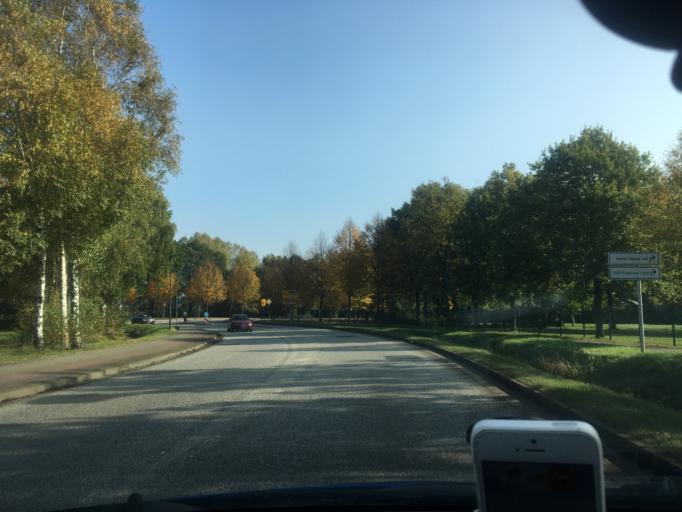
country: DE
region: Mecklenburg-Vorpommern
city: Hagenow
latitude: 53.4279
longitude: 11.2040
